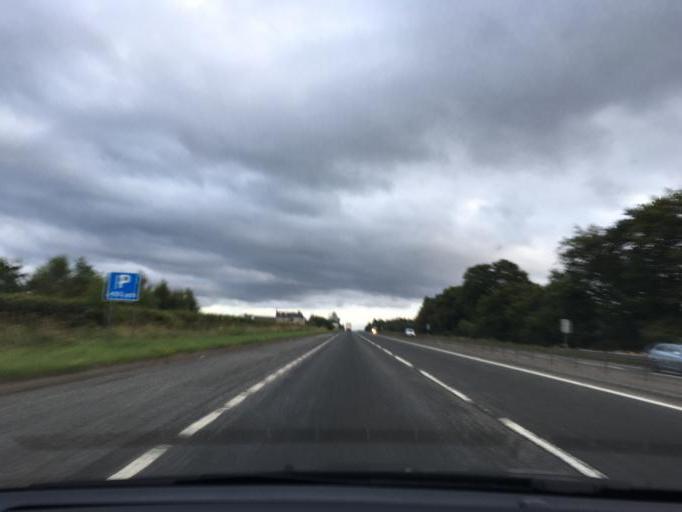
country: GB
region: Scotland
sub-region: Highland
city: Inverness
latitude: 57.4504
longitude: -4.1569
